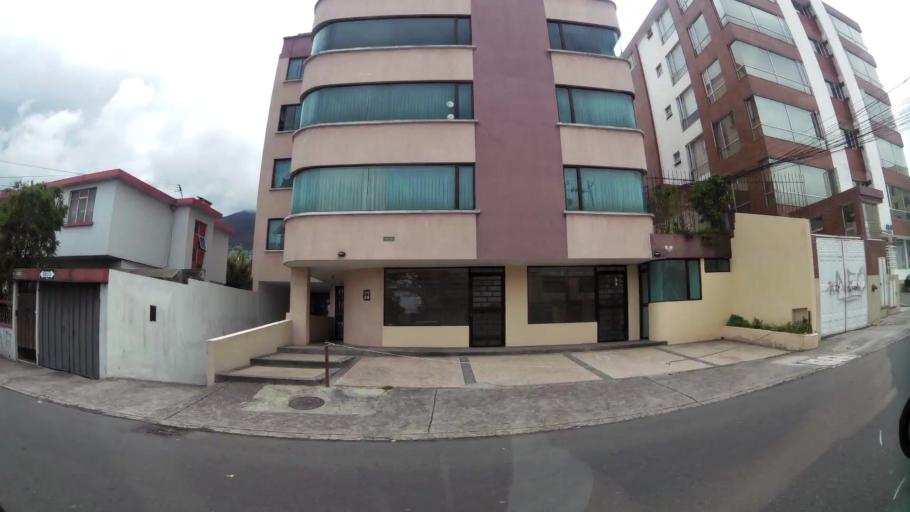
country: EC
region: Pichincha
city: Quito
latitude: -0.1501
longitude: -78.4928
